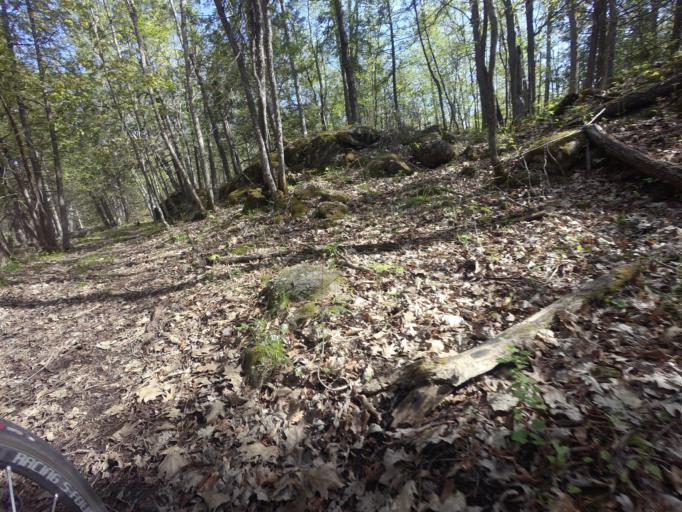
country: CA
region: Ontario
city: Arnprior
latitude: 45.4704
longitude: -76.3003
